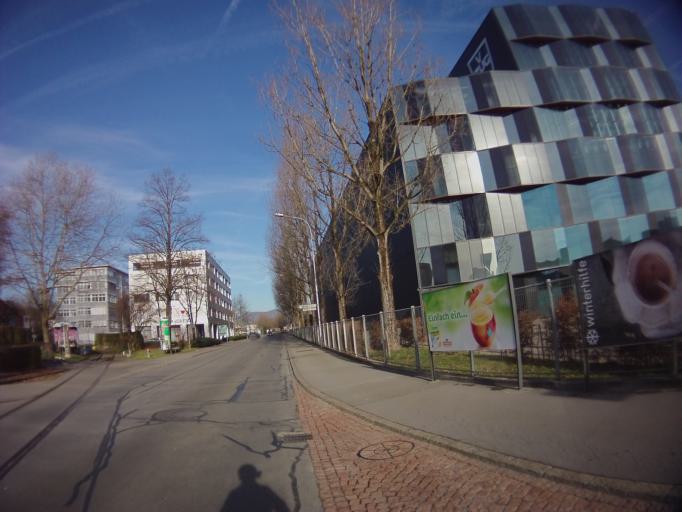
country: CH
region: Zug
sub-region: Zug
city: Zug
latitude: 47.1815
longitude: 8.5214
